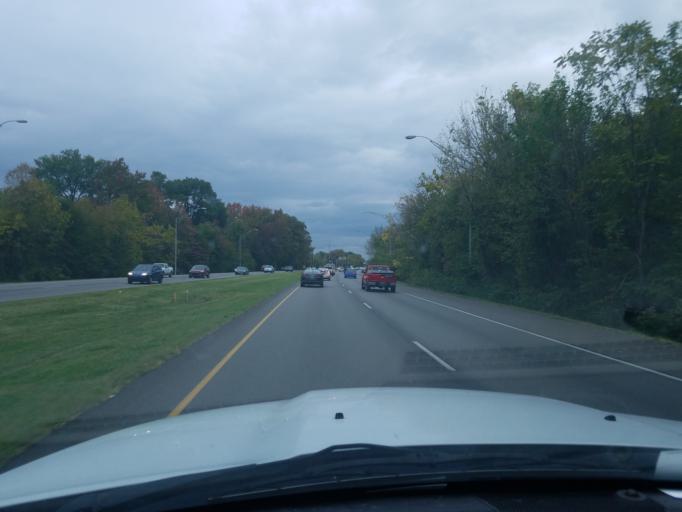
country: US
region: Indiana
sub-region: Vanderburgh County
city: Evansville
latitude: 37.9577
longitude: -87.5427
